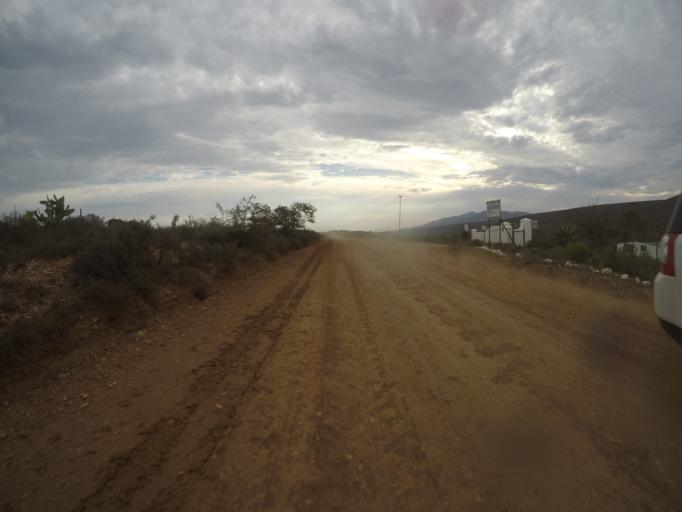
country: ZA
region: Eastern Cape
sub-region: Cacadu District Municipality
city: Willowmore
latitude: -33.4917
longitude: 23.5926
